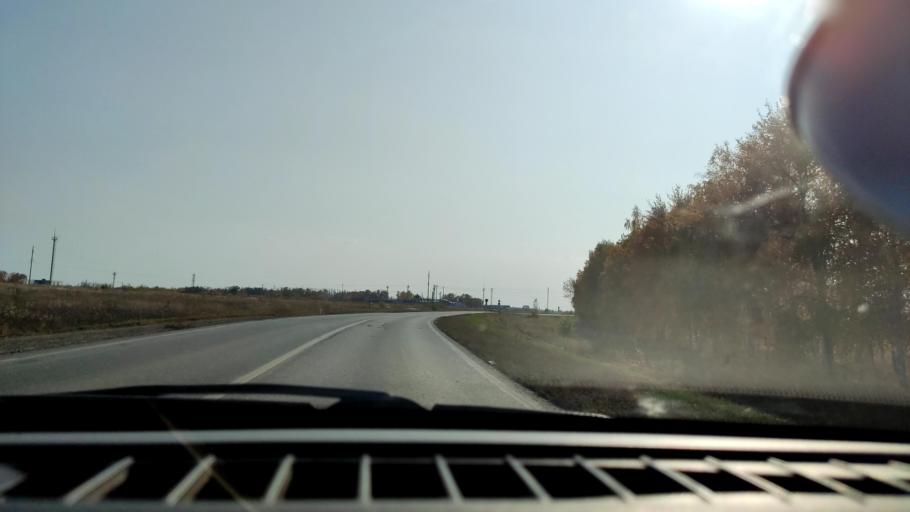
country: RU
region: Samara
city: Dubovyy Umet
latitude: 53.0878
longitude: 50.3492
